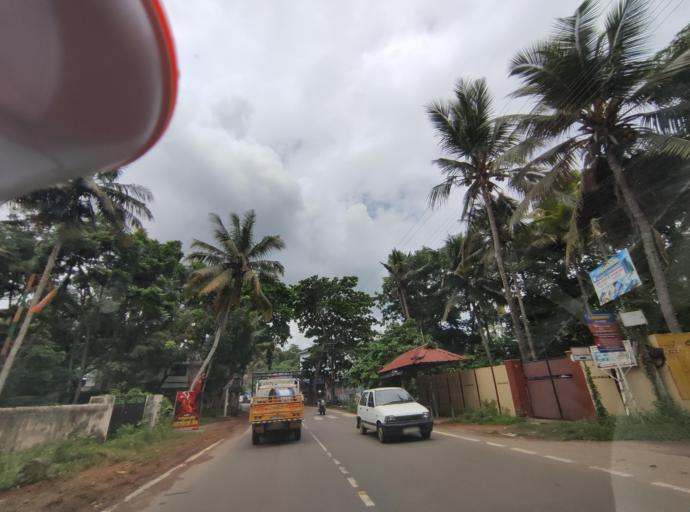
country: IN
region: Kerala
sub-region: Thiruvananthapuram
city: Nedumangad
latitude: 8.5851
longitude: 76.9471
